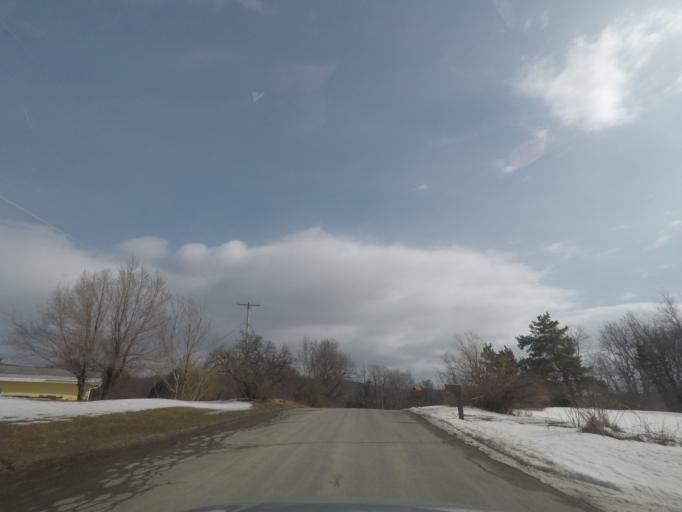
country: US
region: New York
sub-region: Rensselaer County
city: Poestenkill
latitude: 42.7794
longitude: -73.5559
